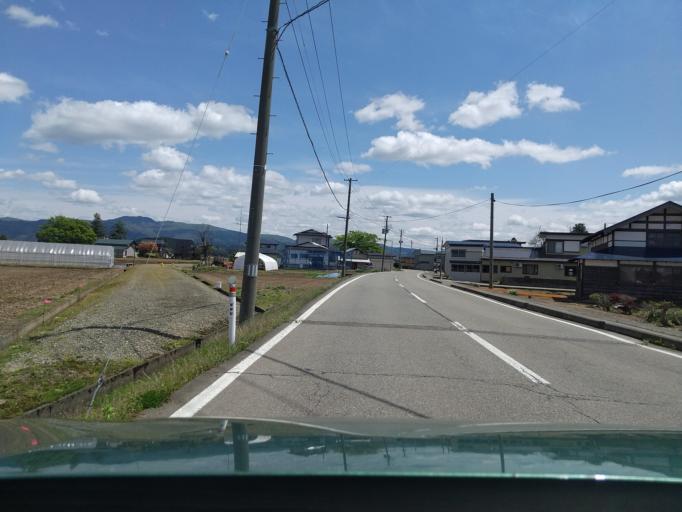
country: JP
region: Akita
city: Omagari
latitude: 39.3845
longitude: 140.5157
